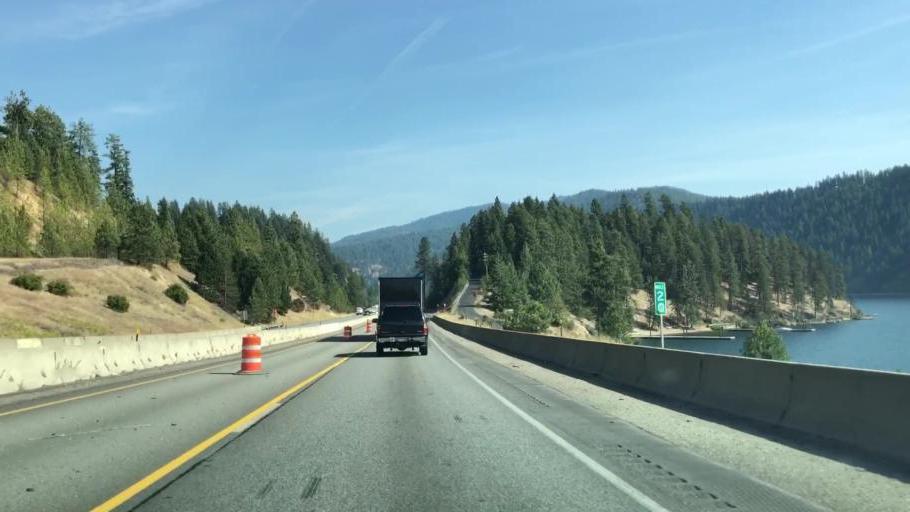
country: US
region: Idaho
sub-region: Kootenai County
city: Coeur d'Alene
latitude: 47.6298
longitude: -116.6850
